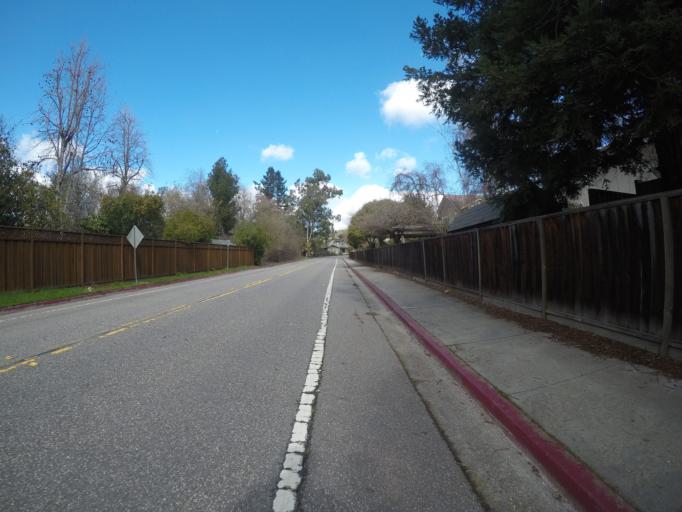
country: US
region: California
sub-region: Santa Cruz County
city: Scotts Valley
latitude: 37.0666
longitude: -122.0041
